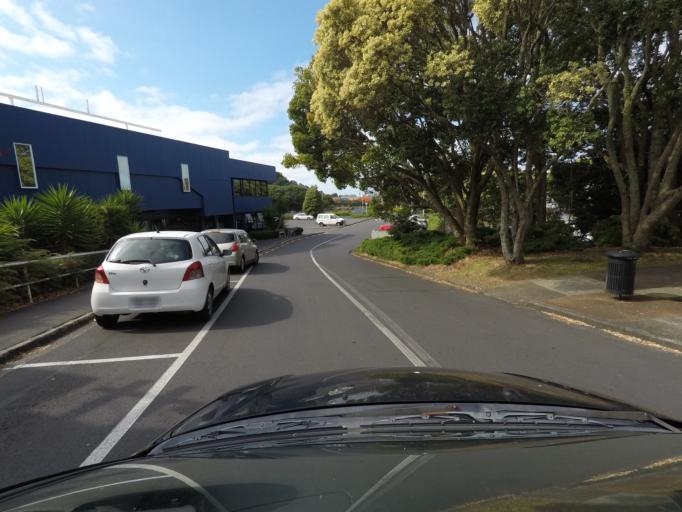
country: NZ
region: Auckland
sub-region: Auckland
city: Auckland
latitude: -36.9086
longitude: 174.7561
